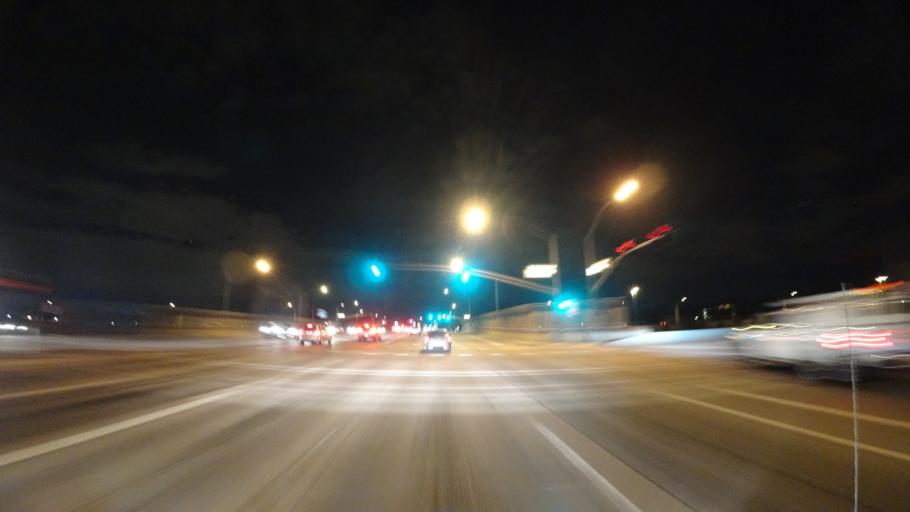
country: US
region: Arizona
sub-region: Maricopa County
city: Chandler
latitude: 33.2864
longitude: -111.8588
